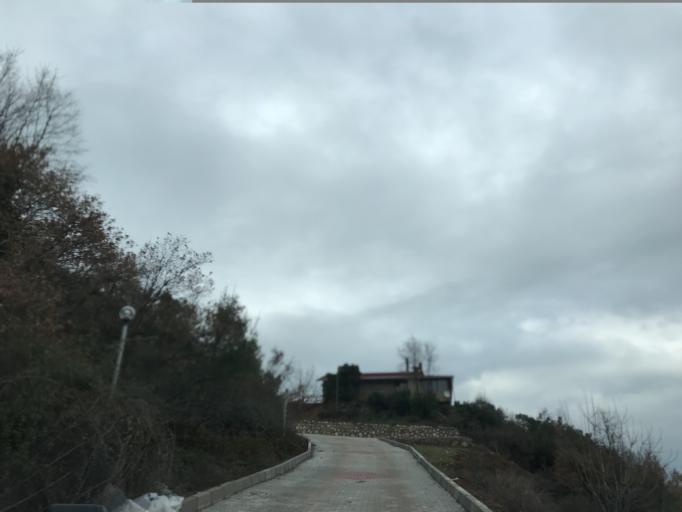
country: TR
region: Yalova
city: Termal
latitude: 40.5976
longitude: 29.1694
